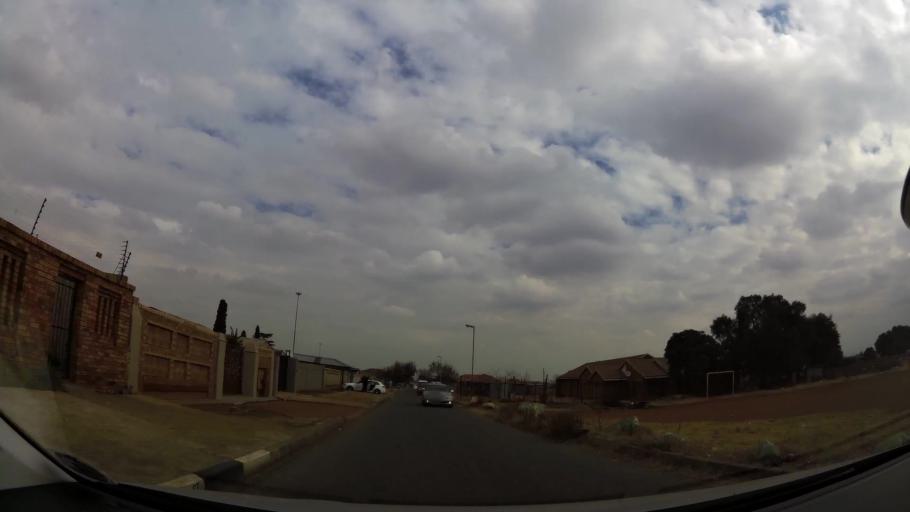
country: ZA
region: Gauteng
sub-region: City of Johannesburg Metropolitan Municipality
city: Soweto
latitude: -26.2609
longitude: 27.8530
